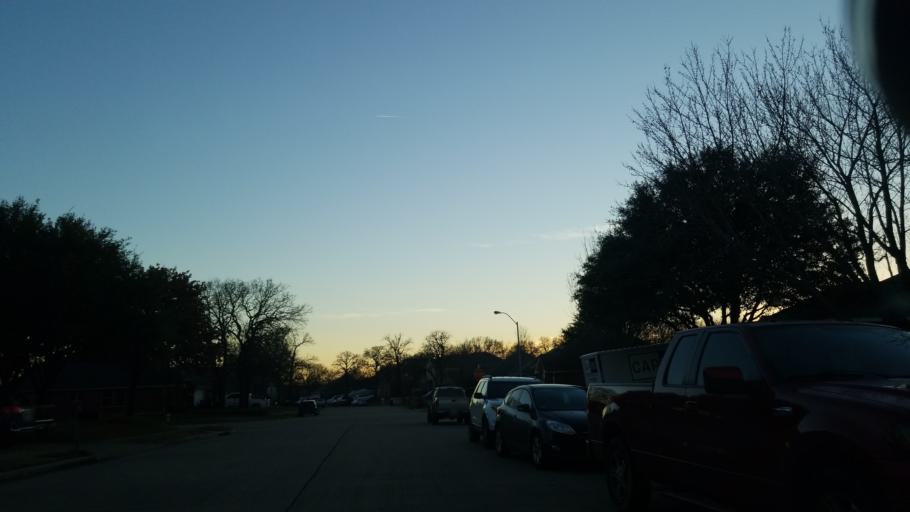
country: US
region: Texas
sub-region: Denton County
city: Corinth
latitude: 33.1377
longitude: -97.0698
